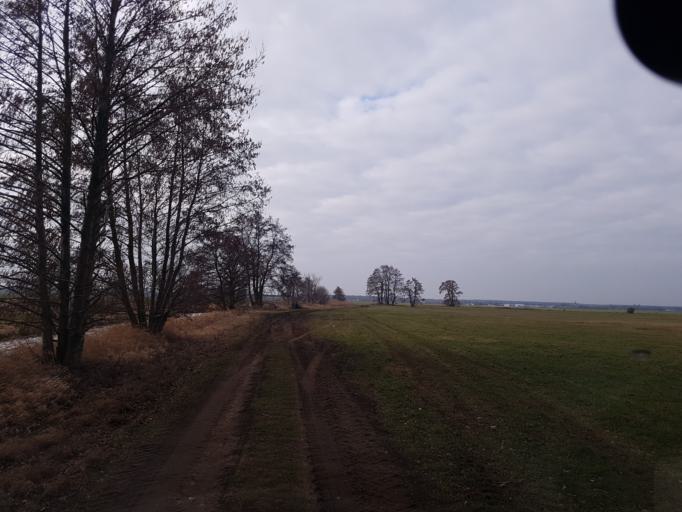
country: DE
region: Brandenburg
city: Schonewalde
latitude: 51.6656
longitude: 13.5690
